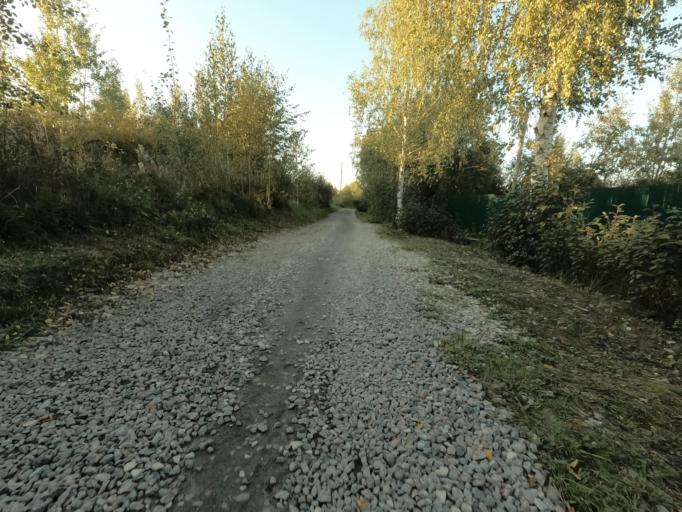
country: RU
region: Leningrad
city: Nikol'skoye
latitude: 59.7084
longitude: 30.7971
